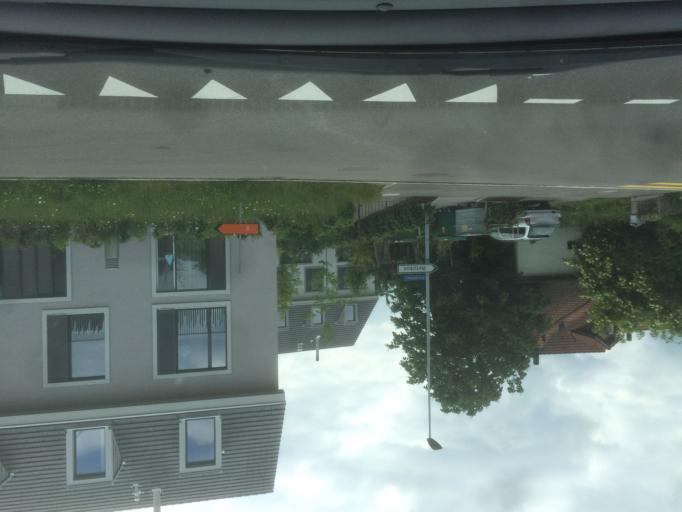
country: CH
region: Zurich
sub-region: Bezirk Hinwil
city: Wetzikon / Robenhausen
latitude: 47.3343
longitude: 8.7772
